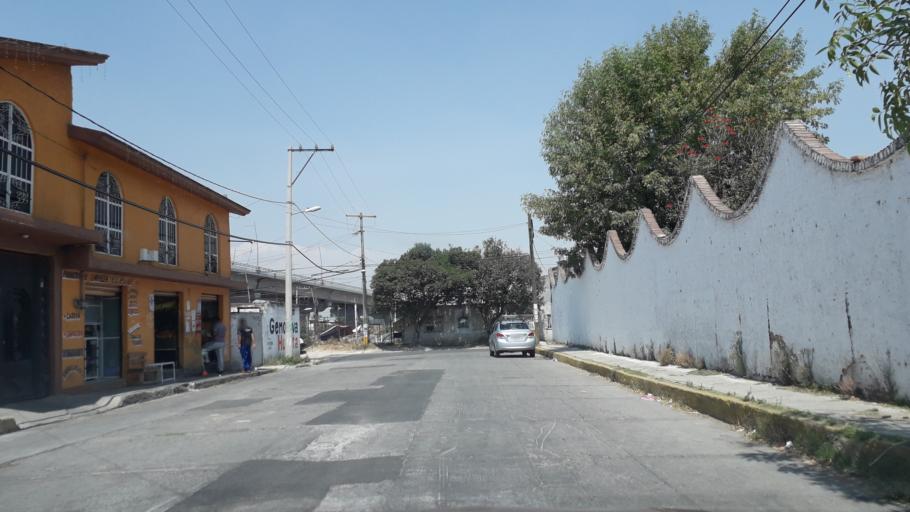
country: MX
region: Puebla
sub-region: Cuautlancingo
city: Sanctorum
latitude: 19.0921
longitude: -98.2211
